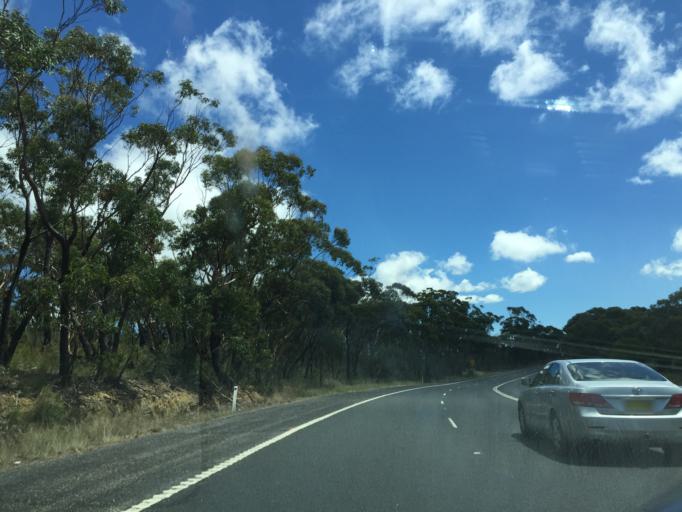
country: AU
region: New South Wales
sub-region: Blue Mountains Municipality
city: Blackheath
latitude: -33.5718
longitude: 150.3586
